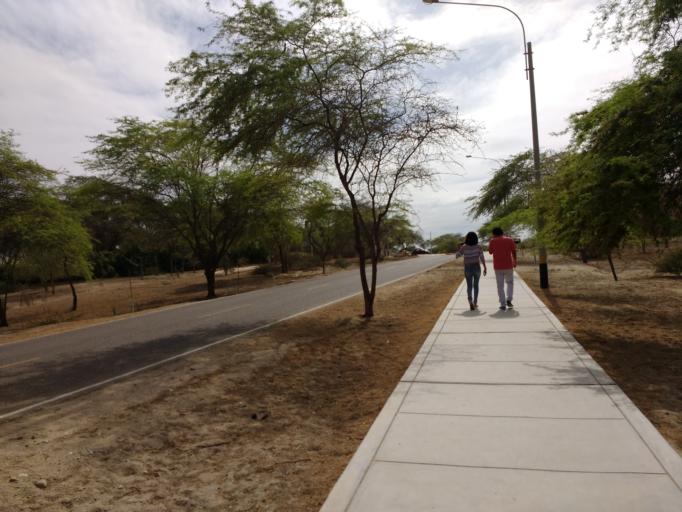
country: PE
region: Piura
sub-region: Provincia de Piura
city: Piura
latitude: -5.1801
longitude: -80.6347
